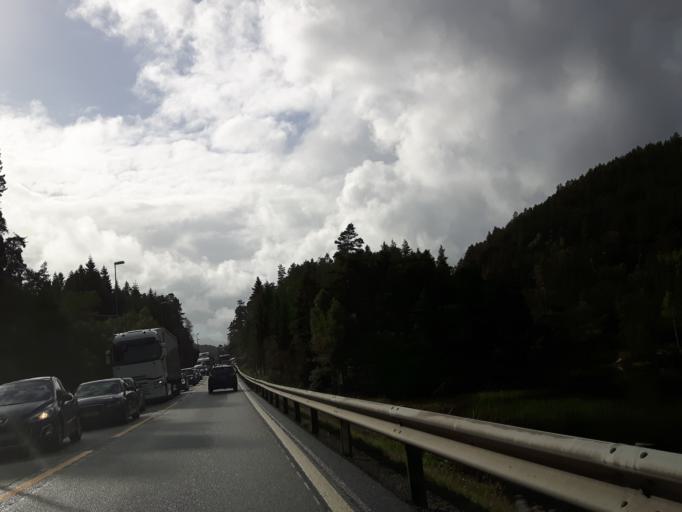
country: NO
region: Vest-Agder
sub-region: Flekkefjord
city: Flekkefjord
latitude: 58.3879
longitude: 6.6291
